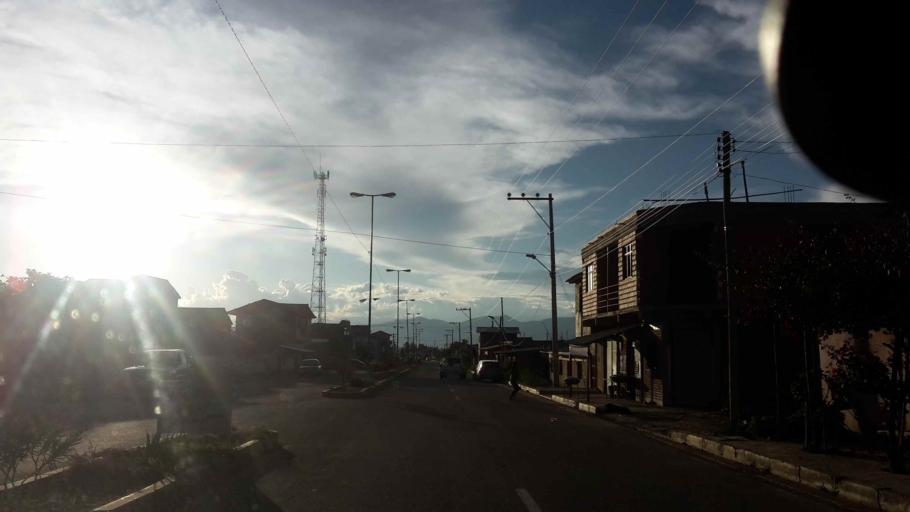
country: BO
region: Cochabamba
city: Arani
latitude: -17.5703
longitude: -65.7696
